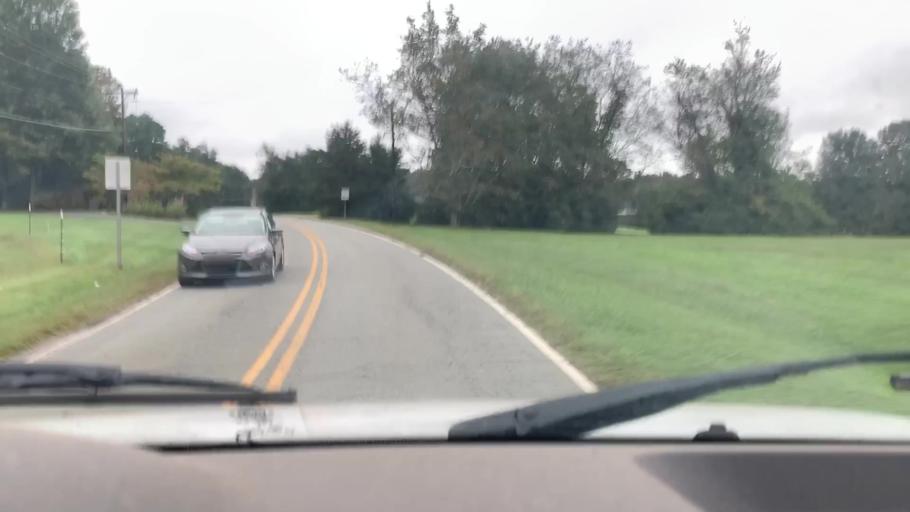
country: US
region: North Carolina
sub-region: Catawba County
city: Lake Norman of Catawba
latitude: 35.5626
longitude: -80.9020
